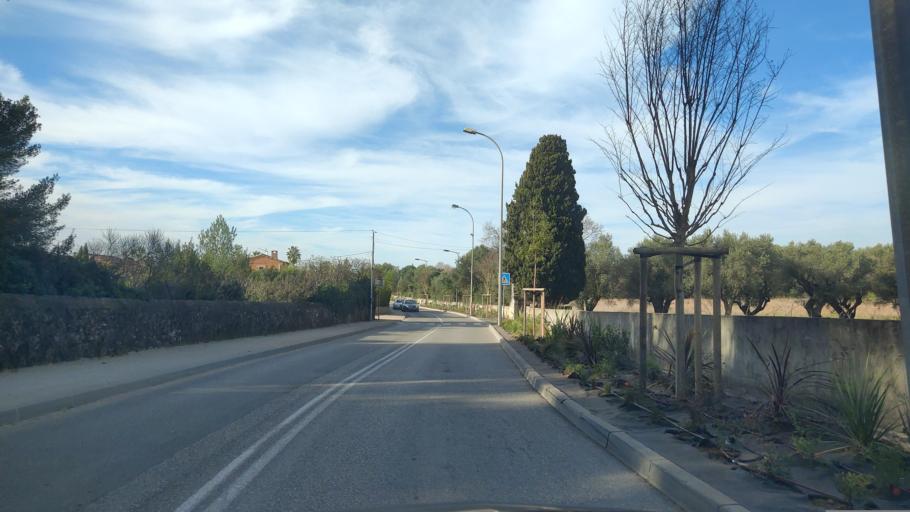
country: FR
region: Provence-Alpes-Cote d'Azur
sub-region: Departement du Var
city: Sanary-sur-Mer
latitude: 43.1275
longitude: 5.8110
